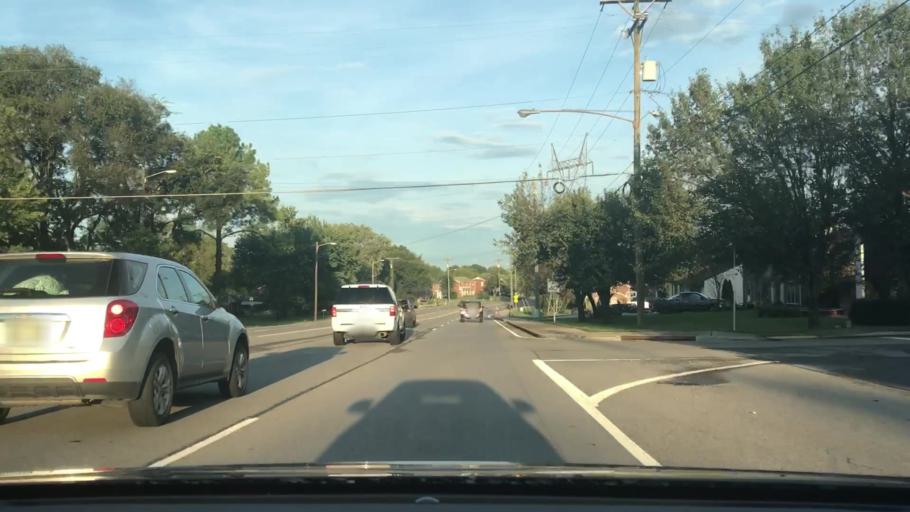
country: US
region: Tennessee
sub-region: Davidson County
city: Oak Hill
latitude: 36.0810
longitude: -86.7555
